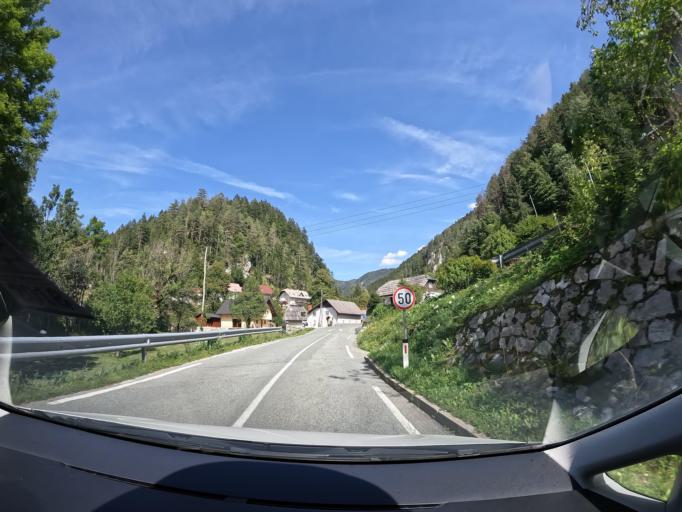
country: SI
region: Jesenice
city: Koroska Bela
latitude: 46.4547
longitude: 14.1000
